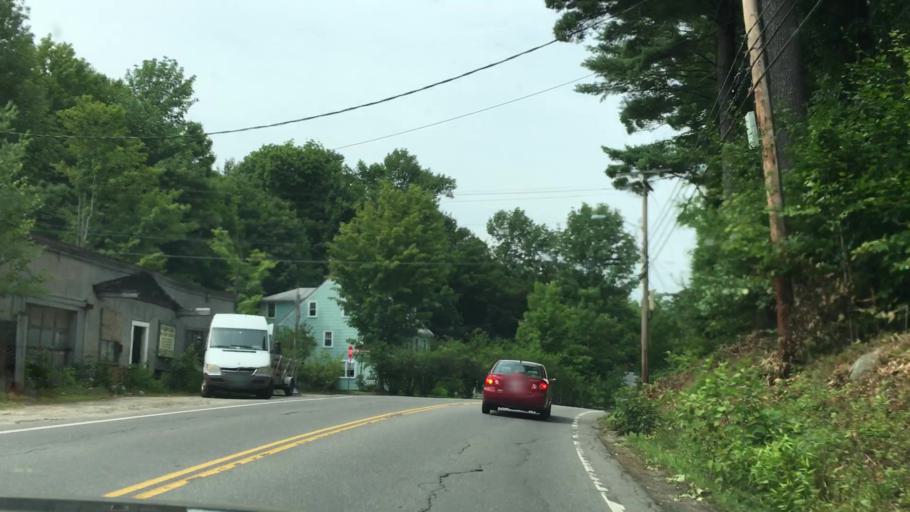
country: US
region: New Hampshire
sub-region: Cheshire County
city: Jaffrey
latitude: 42.8102
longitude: -72.0286
